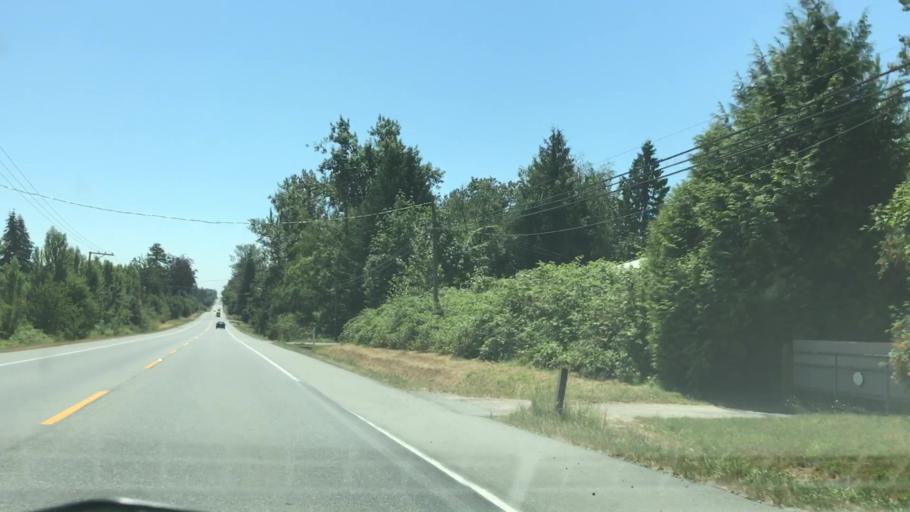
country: CA
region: British Columbia
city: Aldergrove
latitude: 49.0491
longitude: -122.4927
